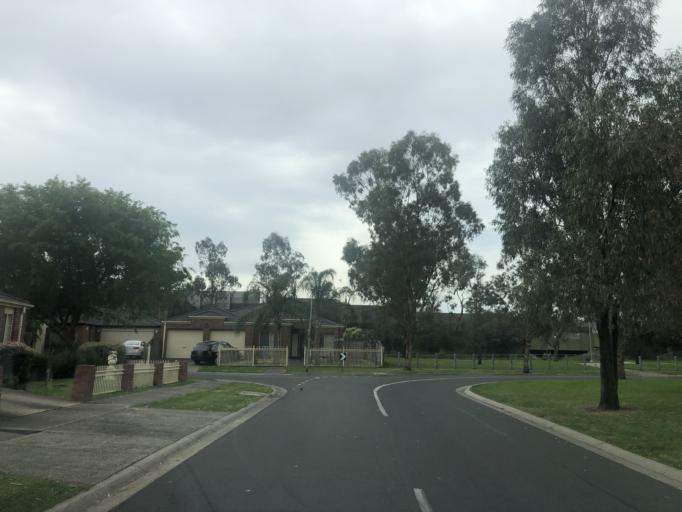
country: AU
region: Victoria
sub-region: Casey
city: Hallam
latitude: -38.0007
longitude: 145.2885
